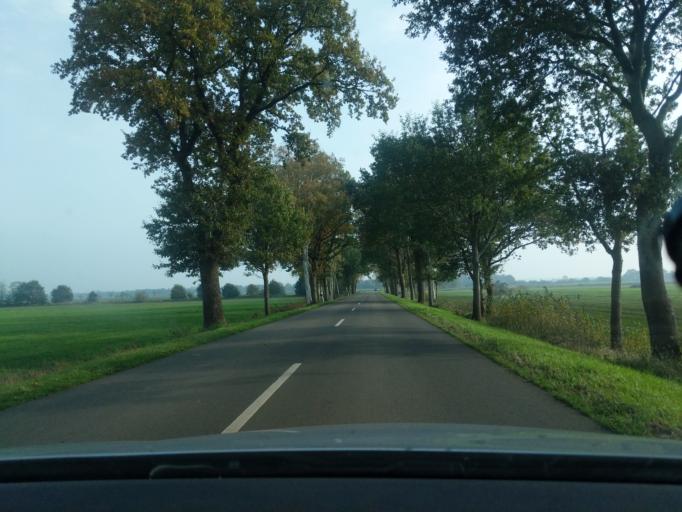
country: DE
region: Lower Saxony
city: Stinstedt
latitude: 53.6538
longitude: 8.9852
